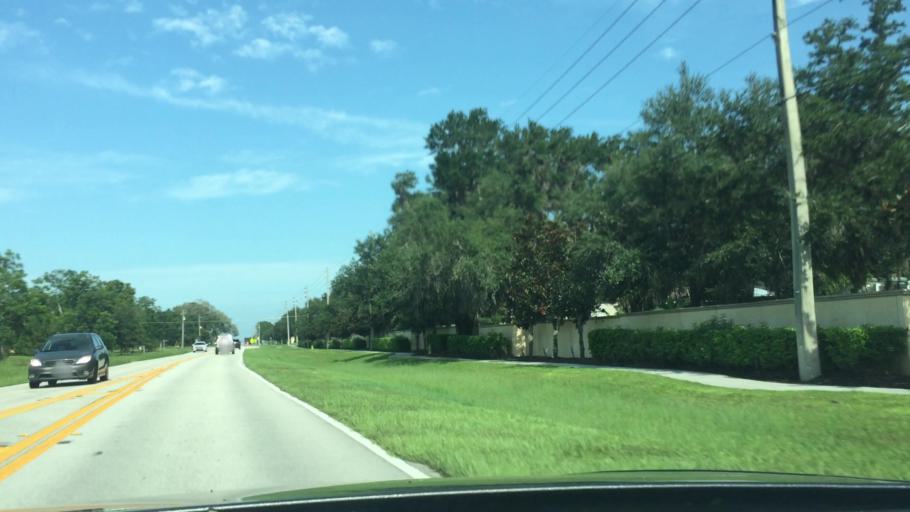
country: US
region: Florida
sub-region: Osceola County
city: Saint Cloud
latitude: 28.2791
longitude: -81.3227
